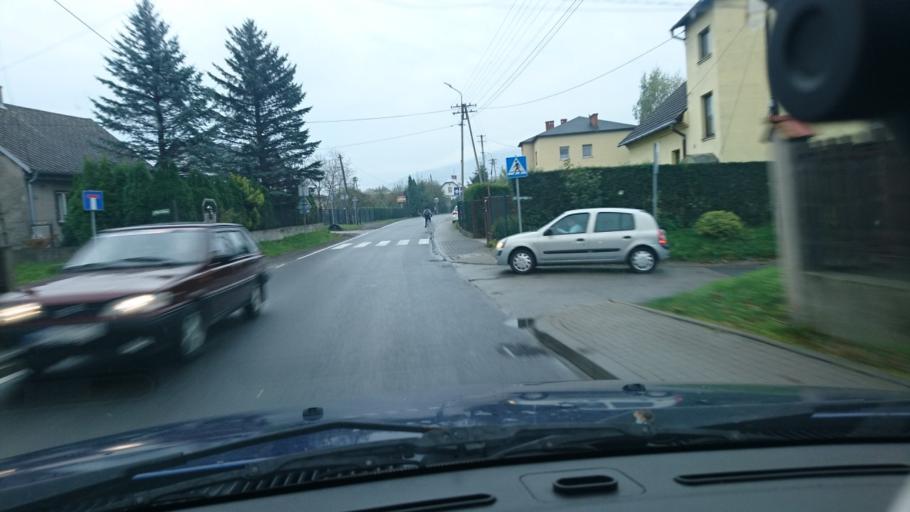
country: PL
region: Silesian Voivodeship
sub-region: Powiat bielski
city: Kozy
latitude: 49.8534
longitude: 19.1401
